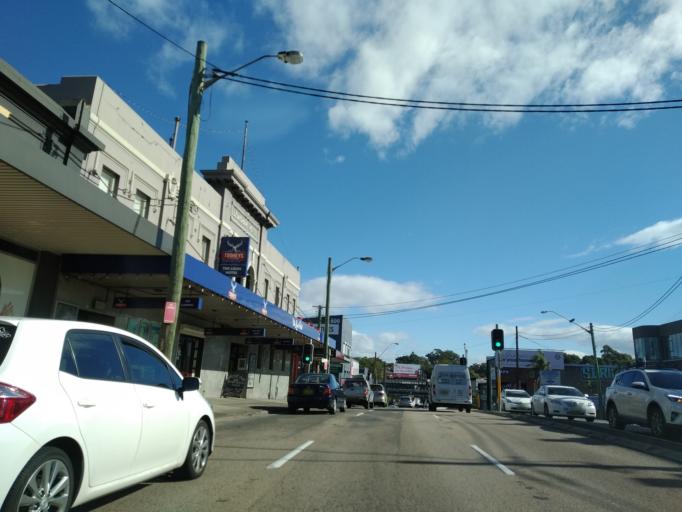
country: AU
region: New South Wales
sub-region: Marrickville
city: Lewisham
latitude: -33.8901
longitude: 151.1471
